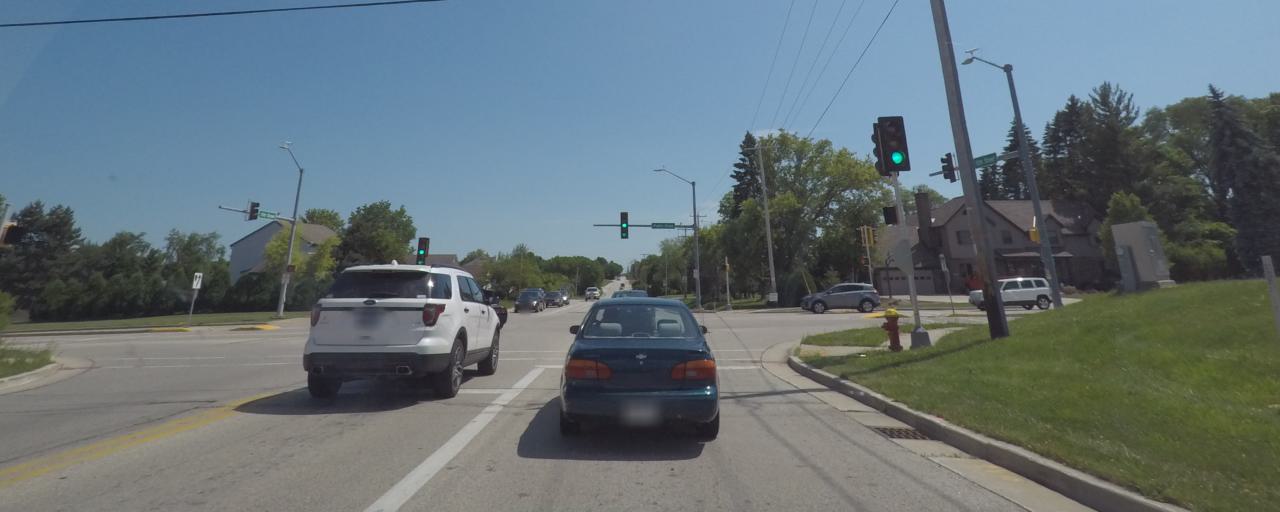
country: US
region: Wisconsin
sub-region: Milwaukee County
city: Oak Creek
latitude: 42.8874
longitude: -87.9318
